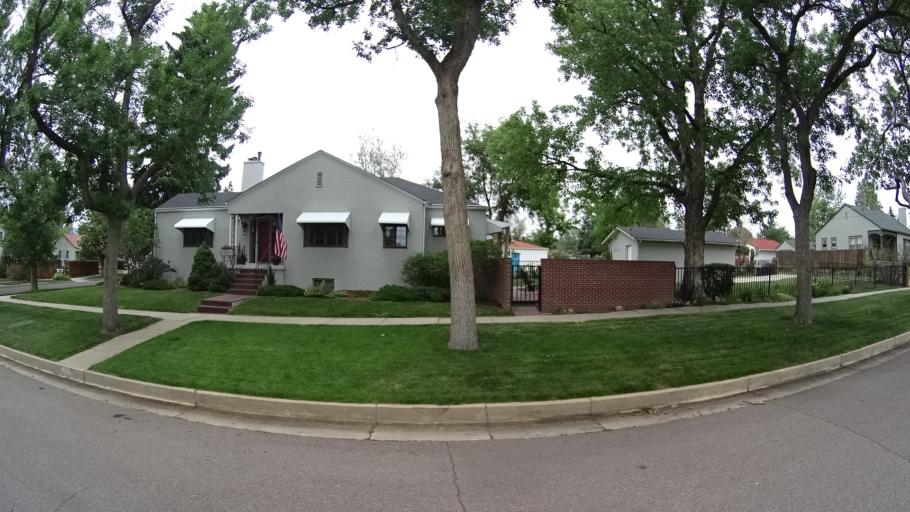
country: US
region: Colorado
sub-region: El Paso County
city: Colorado Springs
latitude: 38.8444
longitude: -104.7982
